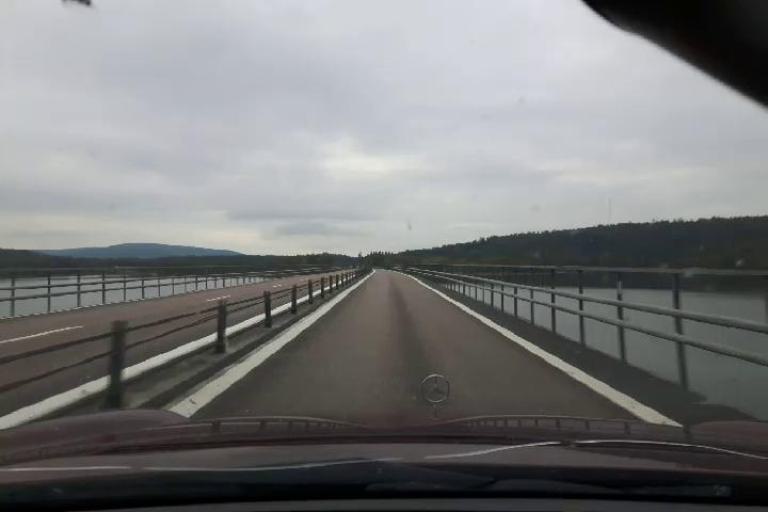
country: SE
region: Vaesternorrland
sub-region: Kramfors Kommun
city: Nordingra
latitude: 62.9054
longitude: 18.0929
